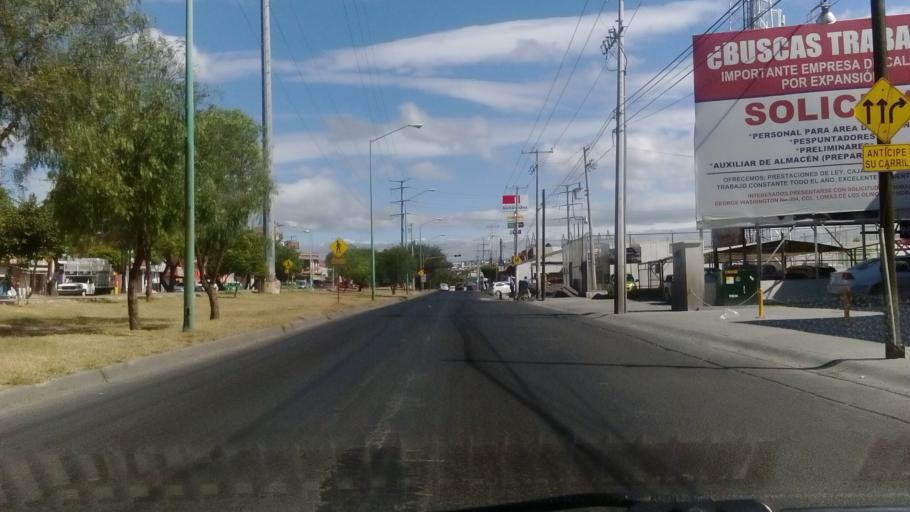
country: MX
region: Guanajuato
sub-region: Leon
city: Ejido la Joya
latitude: 21.1136
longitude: -101.7101
